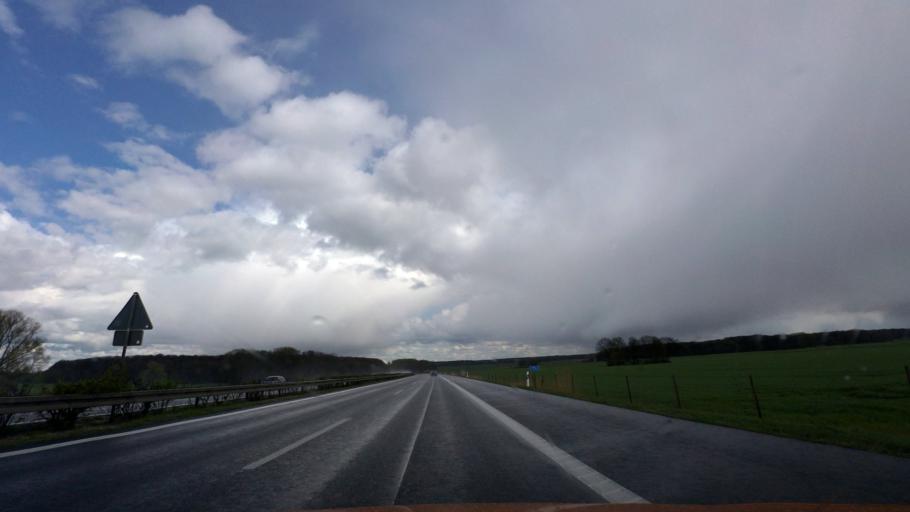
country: DE
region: Mecklenburg-Vorpommern
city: Hagenow
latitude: 53.4861
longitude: 11.1994
